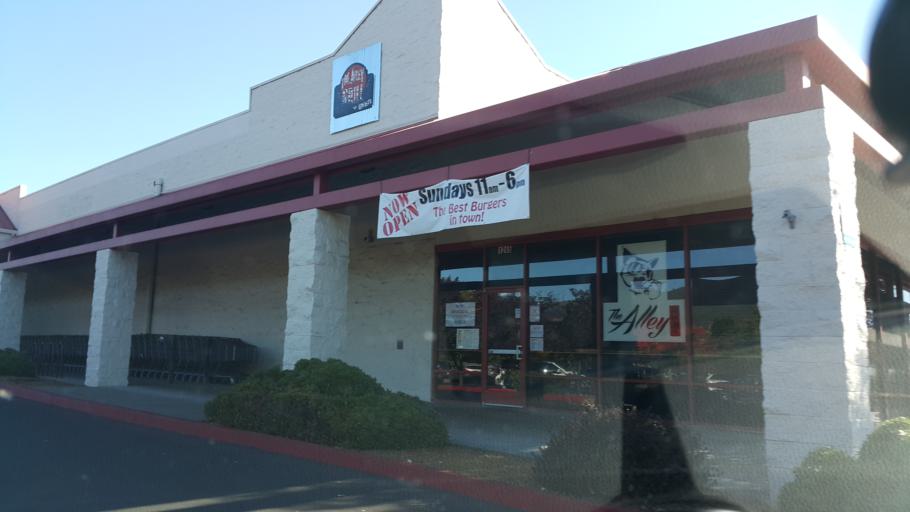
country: US
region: California
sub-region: Mendocino County
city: Ukiah
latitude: 39.1308
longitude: -123.1971
